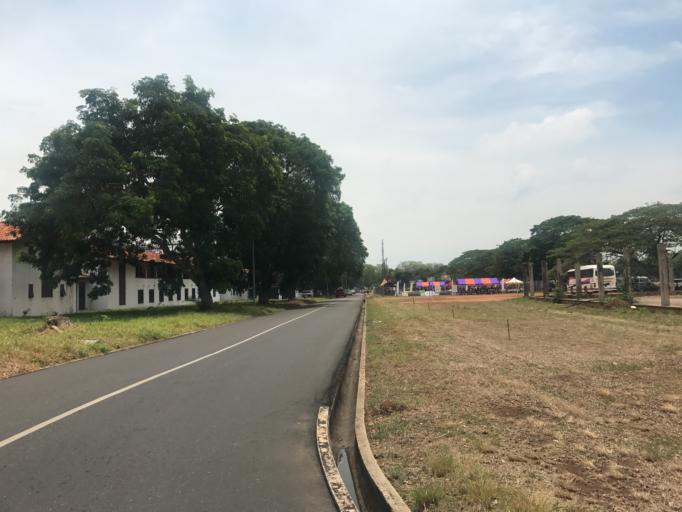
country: GH
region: Greater Accra
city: Medina Estates
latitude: 5.6496
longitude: -0.1862
